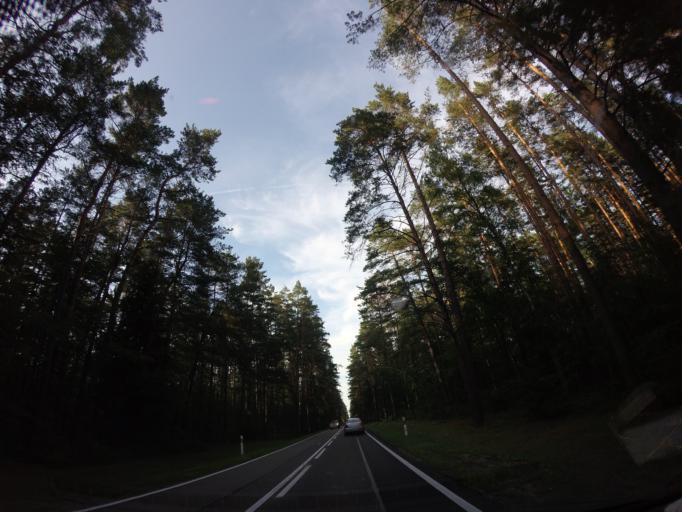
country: PL
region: Podlasie
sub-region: Powiat augustowski
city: Augustow
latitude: 53.8703
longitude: 23.0963
